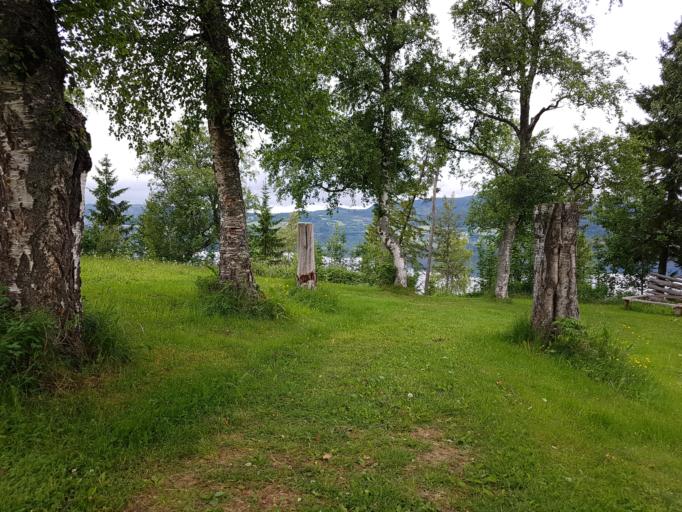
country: NO
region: Sor-Trondelag
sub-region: Selbu
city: Mebonden
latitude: 63.2349
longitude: 11.0284
